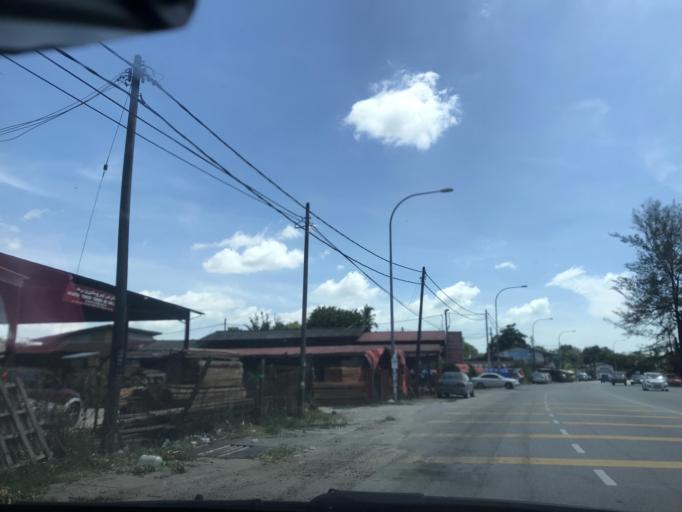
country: MY
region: Kelantan
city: Kota Bharu
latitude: 6.1098
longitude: 102.2632
